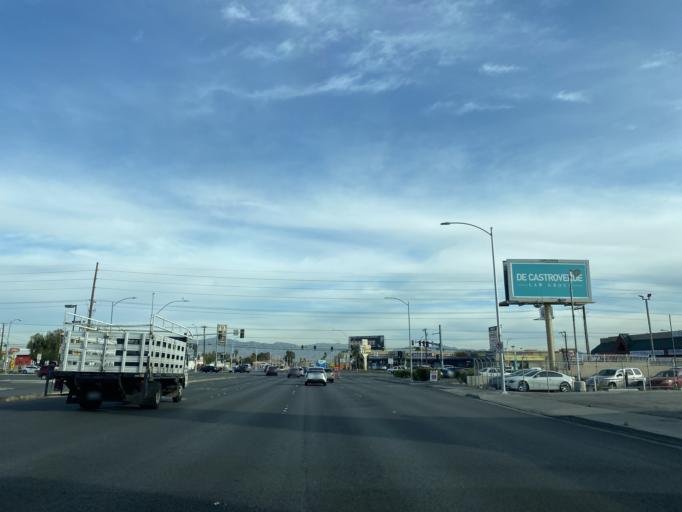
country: US
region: Nevada
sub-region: Clark County
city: Winchester
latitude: 36.1432
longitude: -115.1187
